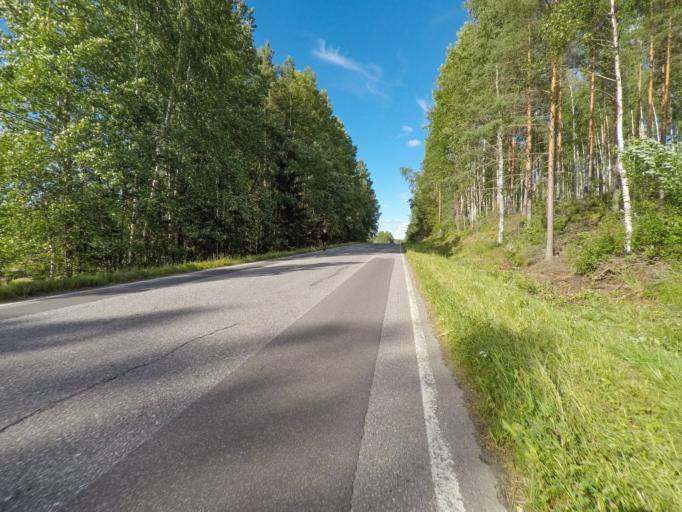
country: FI
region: South Karelia
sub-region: Imatra
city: Imatra
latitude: 61.1325
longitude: 28.7273
